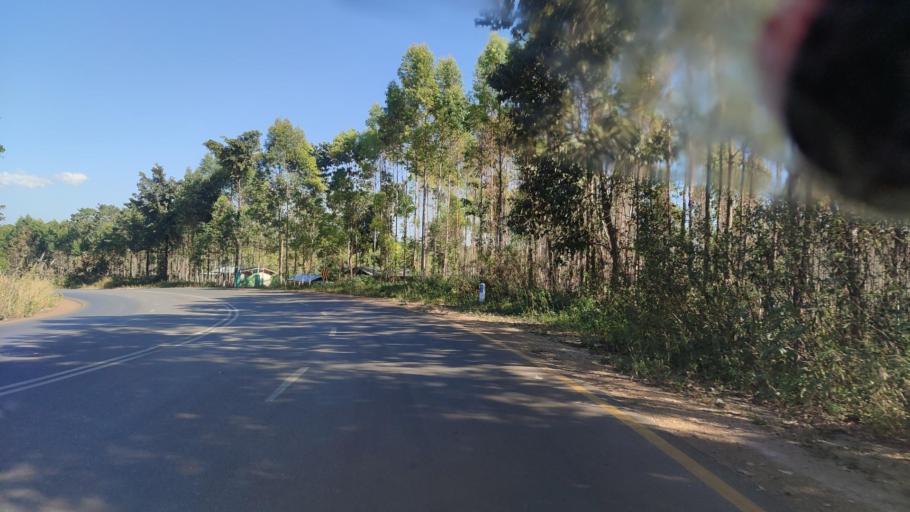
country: MM
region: Mandalay
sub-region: Pyin Oo Lwin District
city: Pyin Oo Lwin
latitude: 22.1620
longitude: 96.6260
